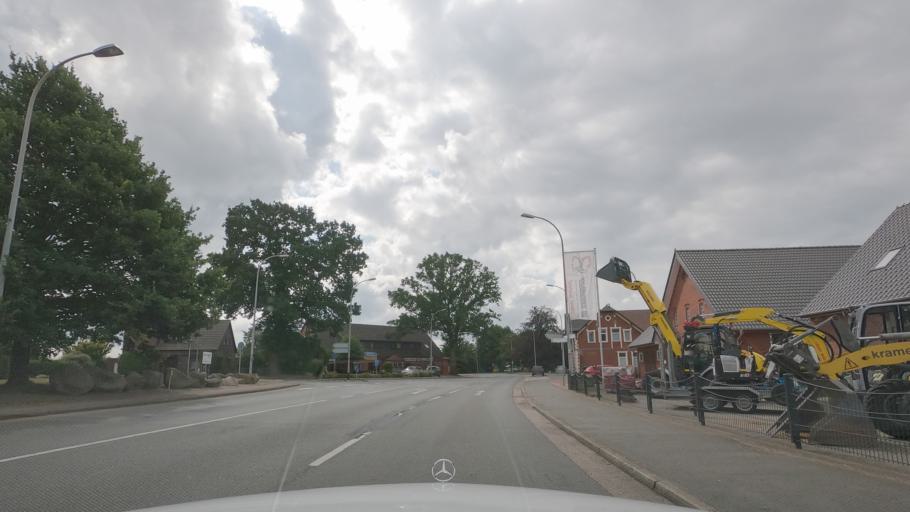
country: DE
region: Lower Saxony
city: Uthlede
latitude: 53.3086
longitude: 8.5798
